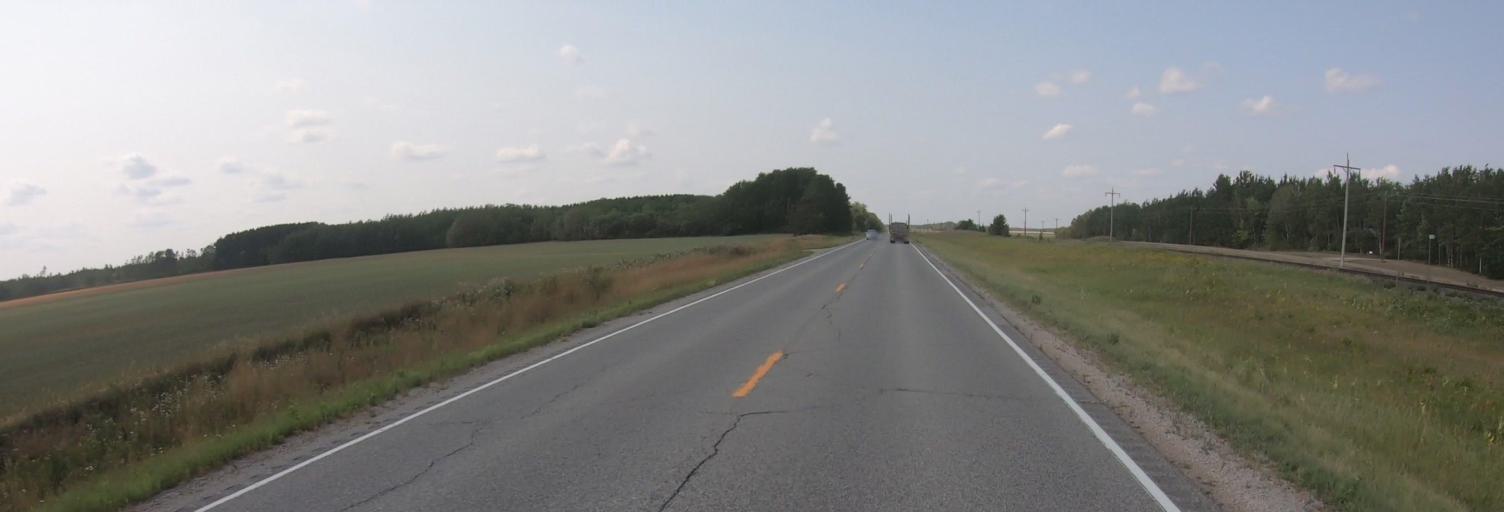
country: US
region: Minnesota
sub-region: Roseau County
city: Warroad
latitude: 48.8372
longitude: -95.1827
